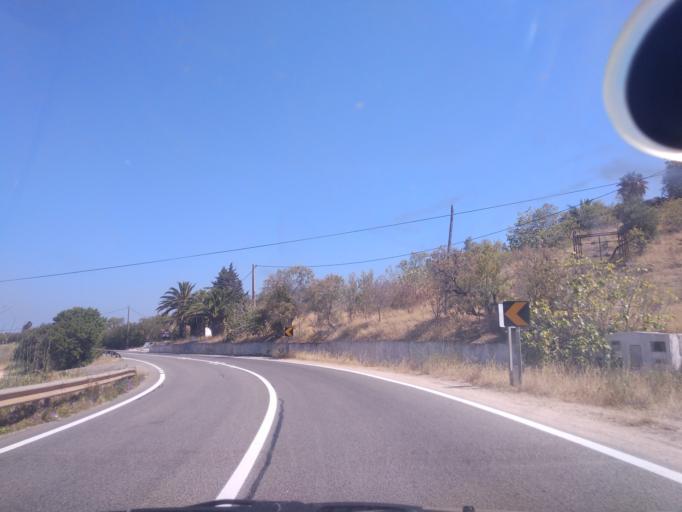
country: PT
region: Faro
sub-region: Lagos
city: Lagos
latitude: 37.1146
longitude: -8.6864
